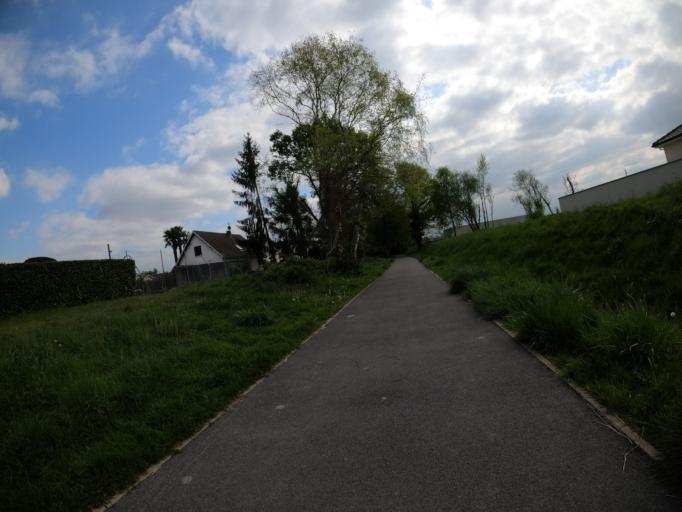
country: FR
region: Aquitaine
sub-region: Departement des Pyrenees-Atlantiques
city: Lons
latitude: 43.3314
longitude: -0.3824
